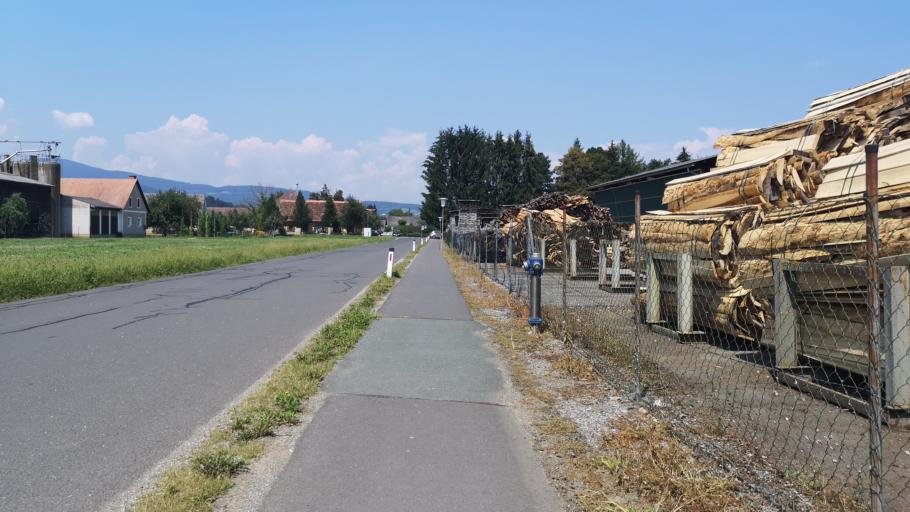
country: AT
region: Styria
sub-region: Politischer Bezirk Deutschlandsberg
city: Deutschlandsberg
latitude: 46.8203
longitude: 15.2559
